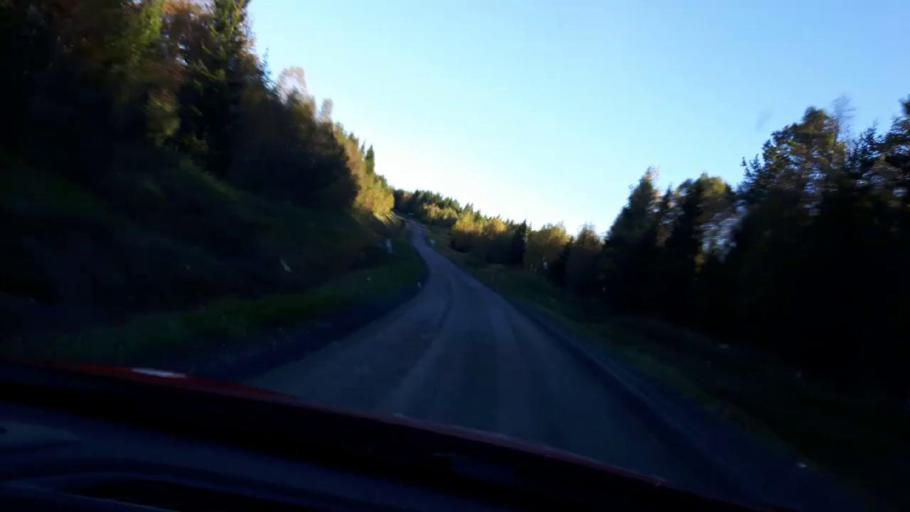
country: SE
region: Jaemtland
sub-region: OEstersunds Kommun
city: Lit
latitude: 63.5752
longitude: 14.8653
